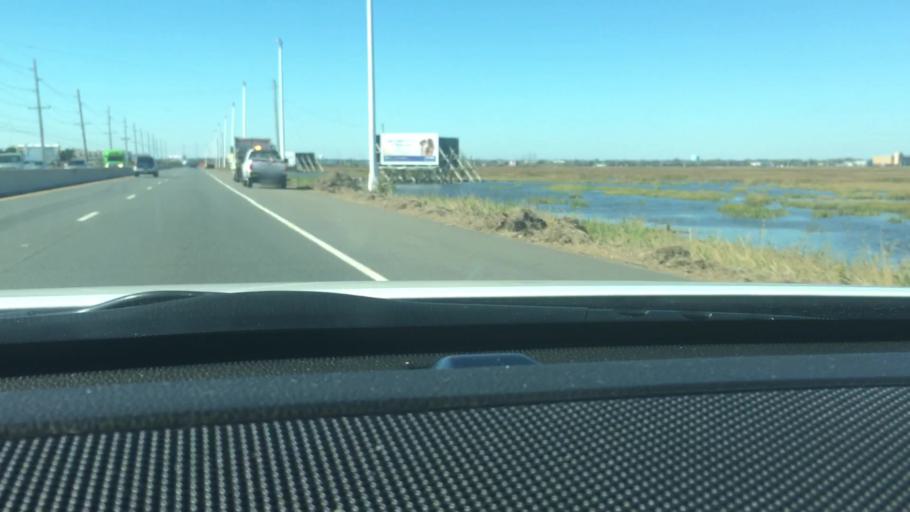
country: US
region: New Jersey
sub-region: Atlantic County
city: Absecon
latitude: 39.3888
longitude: -74.4790
